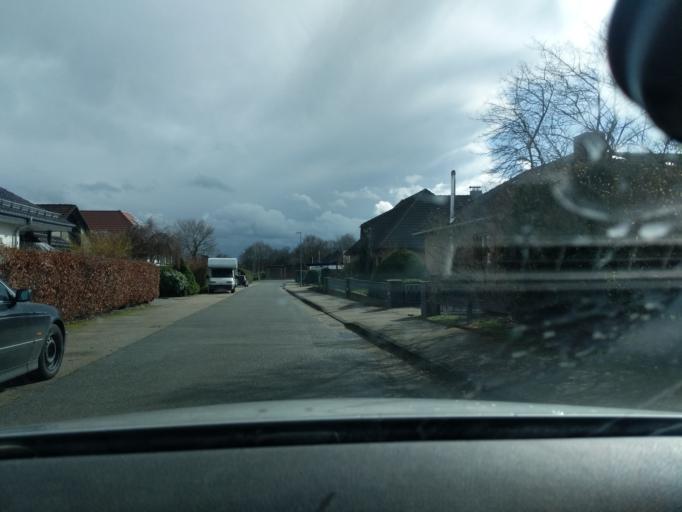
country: DE
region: Lower Saxony
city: Oldendorf
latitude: 53.5877
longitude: 9.2417
